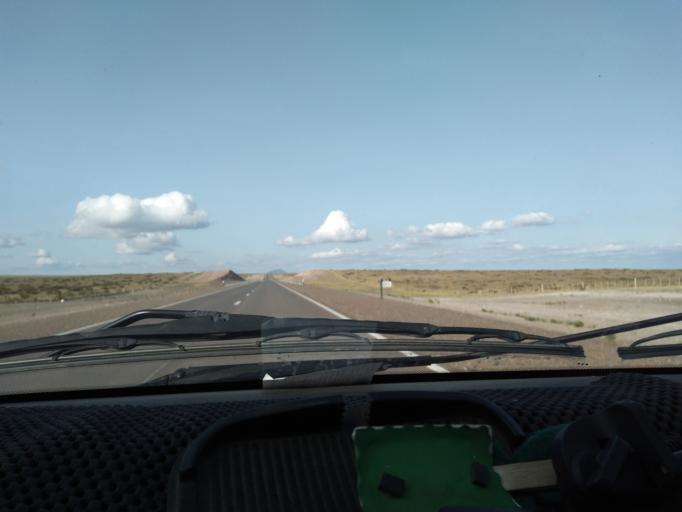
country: AR
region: Mendoza
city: Malargue
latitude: -34.8691
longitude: -69.3041
